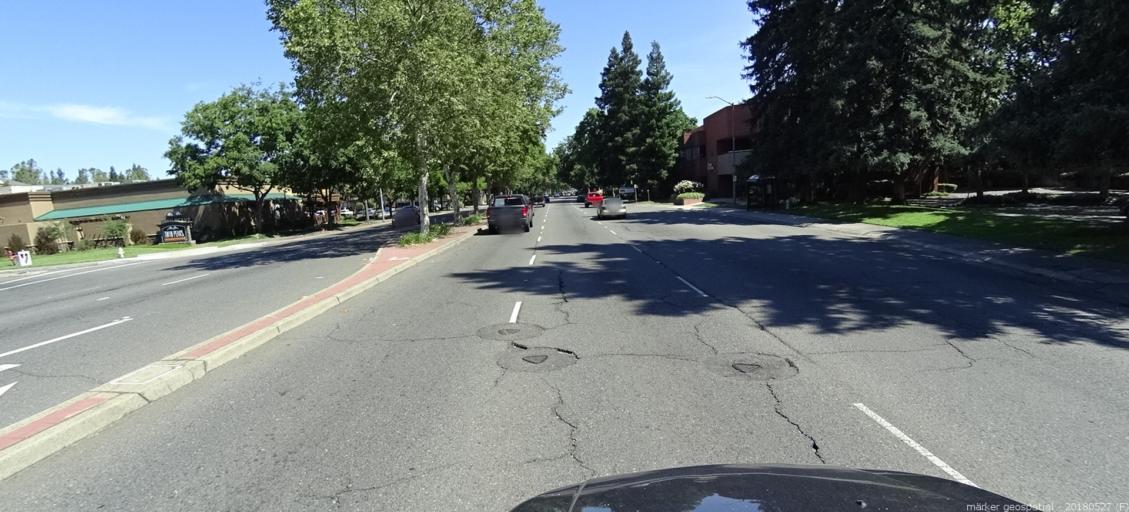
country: US
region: California
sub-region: Sacramento County
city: Arden-Arcade
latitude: 38.5751
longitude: -121.4153
